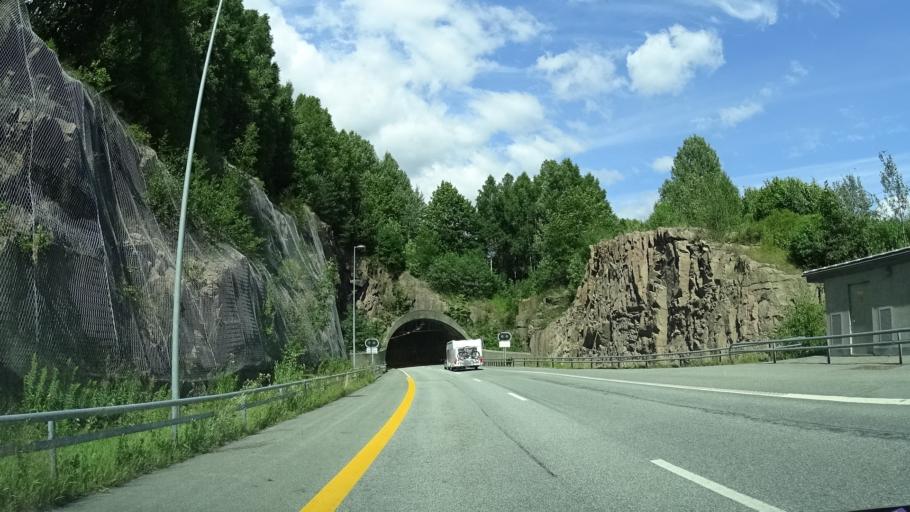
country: NO
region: Buskerud
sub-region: Drammen
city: Skoger
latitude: 59.7224
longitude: 10.2282
